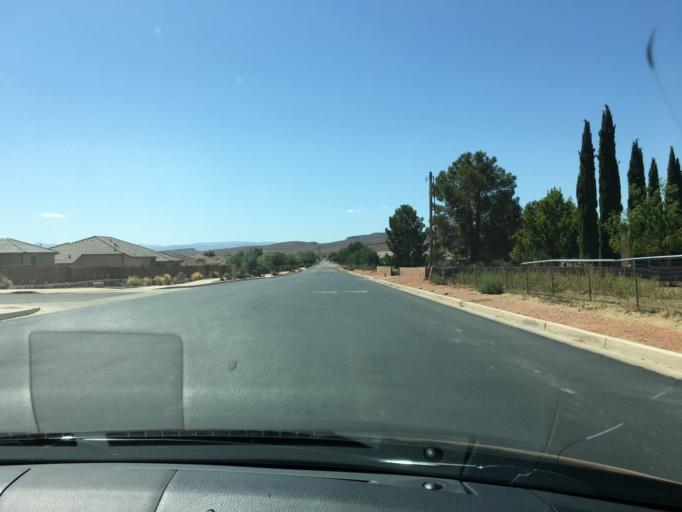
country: US
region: Utah
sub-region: Washington County
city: Ivins
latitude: 37.1672
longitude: -113.6888
